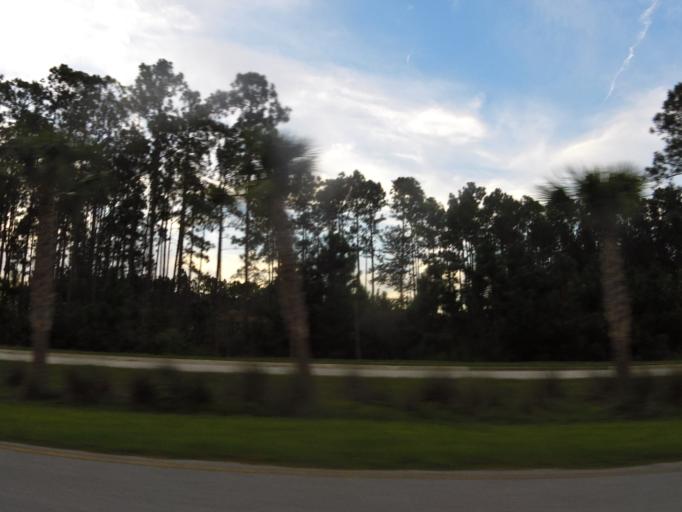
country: US
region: Florida
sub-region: Saint Johns County
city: Fruit Cove
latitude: 30.0864
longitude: -81.5952
